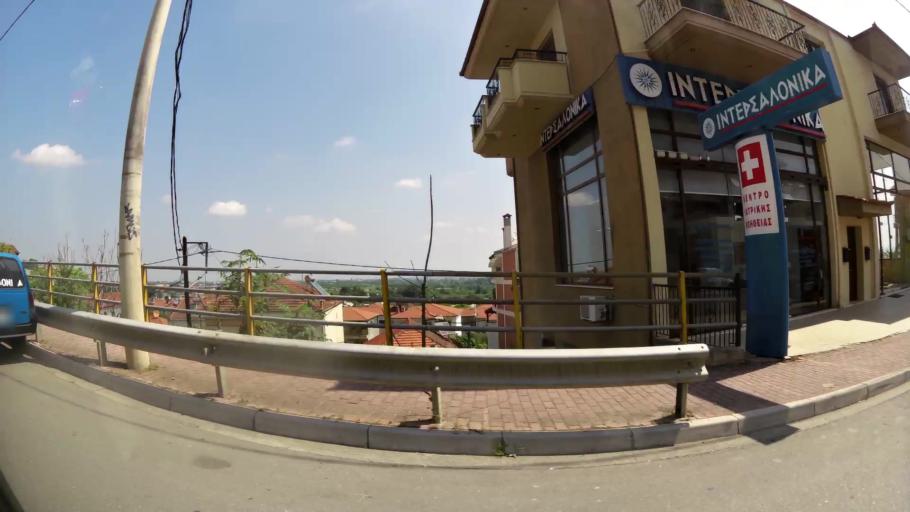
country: GR
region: Central Macedonia
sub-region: Nomos Imathias
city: Veroia
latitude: 40.5126
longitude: 22.2119
